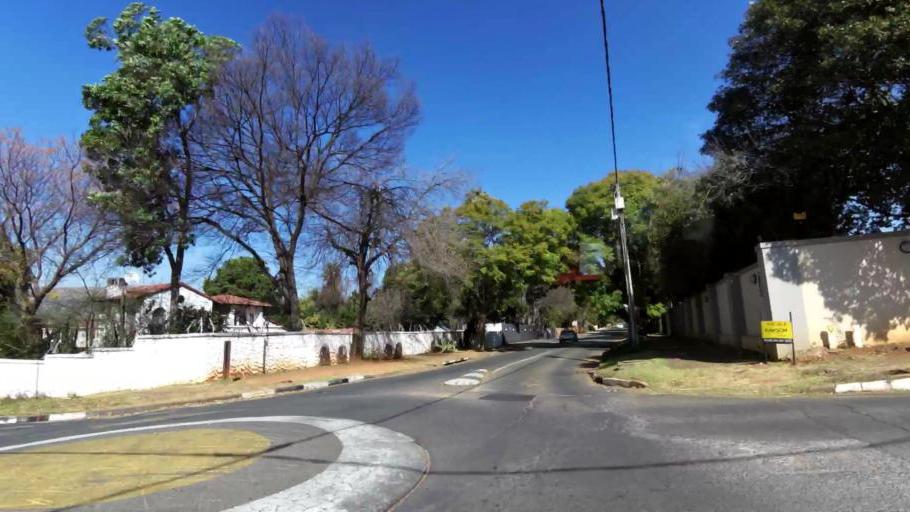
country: ZA
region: Gauteng
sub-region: City of Johannesburg Metropolitan Municipality
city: Roodepoort
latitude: -26.1248
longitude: 27.9547
